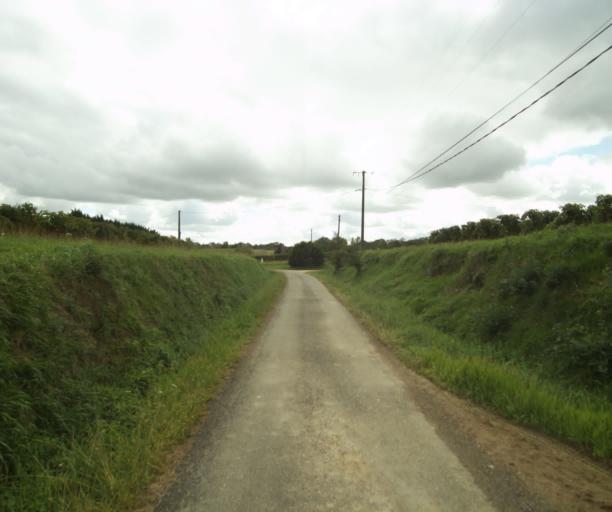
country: FR
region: Midi-Pyrenees
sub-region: Departement du Gers
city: Nogaro
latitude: 43.8317
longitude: -0.0068
